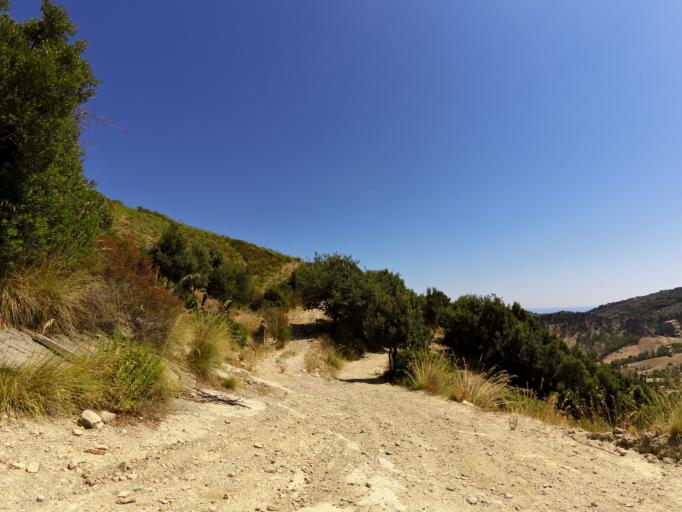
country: IT
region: Calabria
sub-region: Provincia di Reggio Calabria
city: Stilo
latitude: 38.4635
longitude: 16.4602
